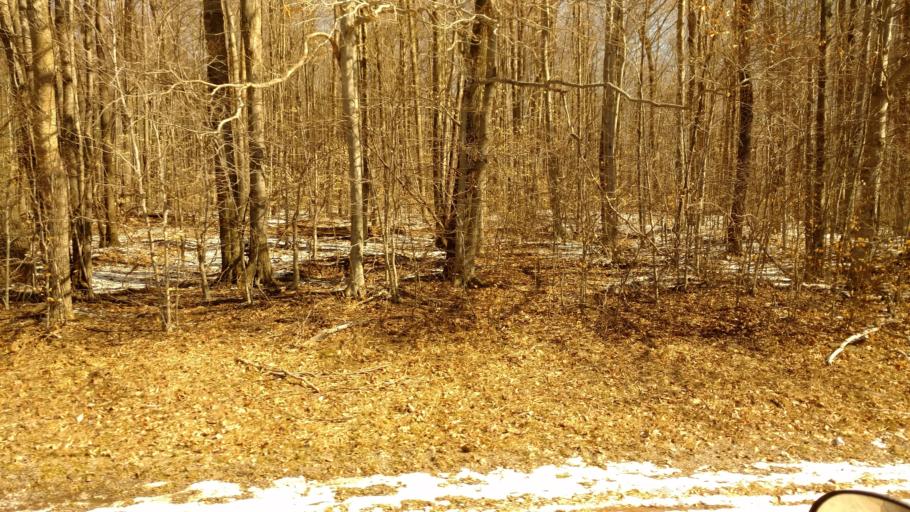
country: US
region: New York
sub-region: Allegany County
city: Wellsville
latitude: 42.0498
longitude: -77.9795
